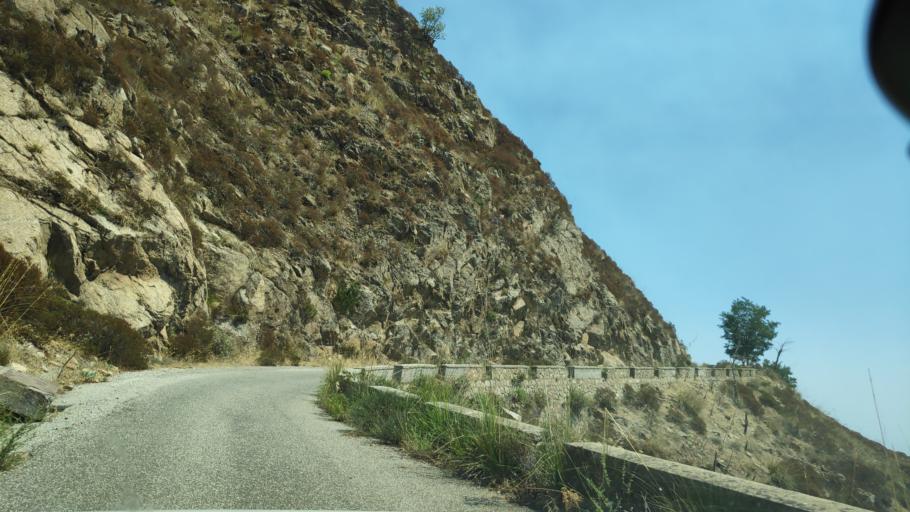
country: IT
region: Calabria
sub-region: Provincia di Reggio Calabria
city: Bova
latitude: 38.0020
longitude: 15.9276
